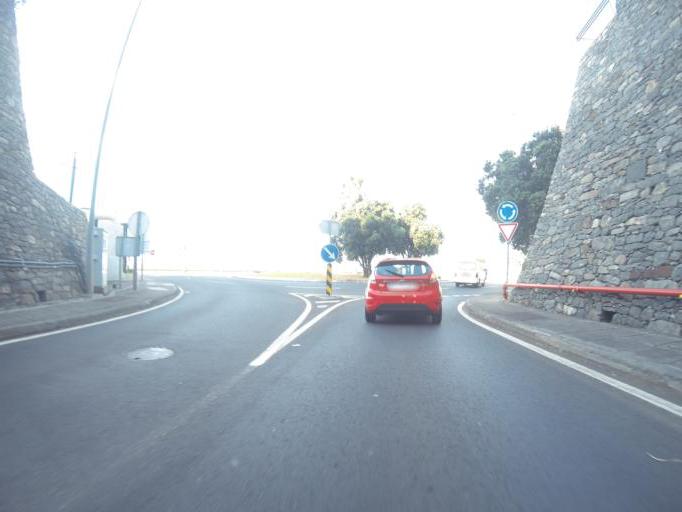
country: PT
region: Madeira
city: Ponta do Sol
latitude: 32.6780
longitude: -17.0807
